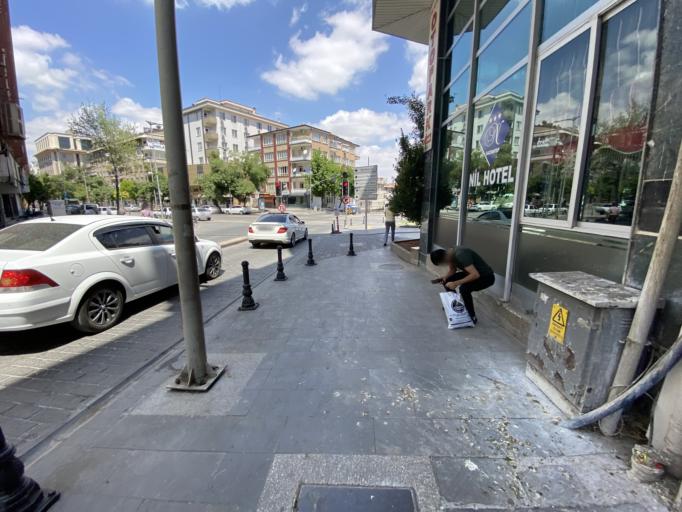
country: TR
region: Gaziantep
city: Gaziantep
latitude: 37.0620
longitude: 37.3754
